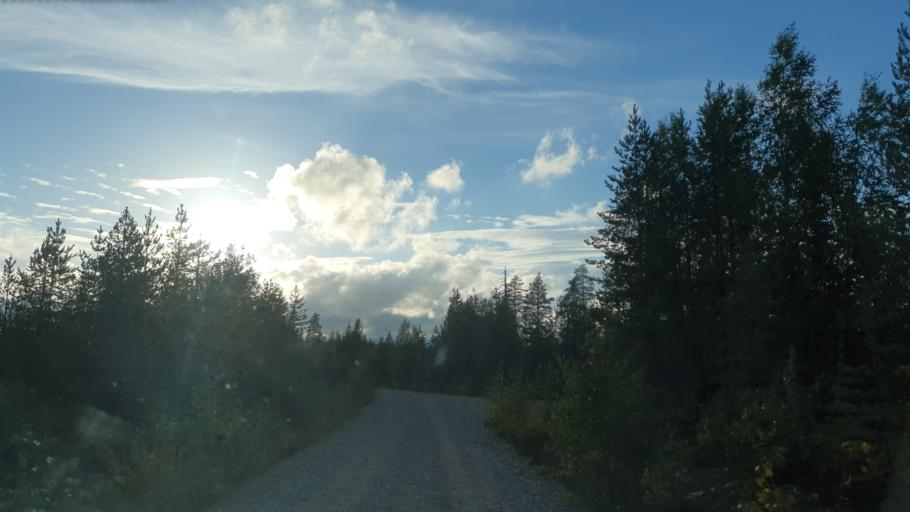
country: FI
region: Kainuu
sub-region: Kehys-Kainuu
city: Kuhmo
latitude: 64.3346
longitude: 30.0067
